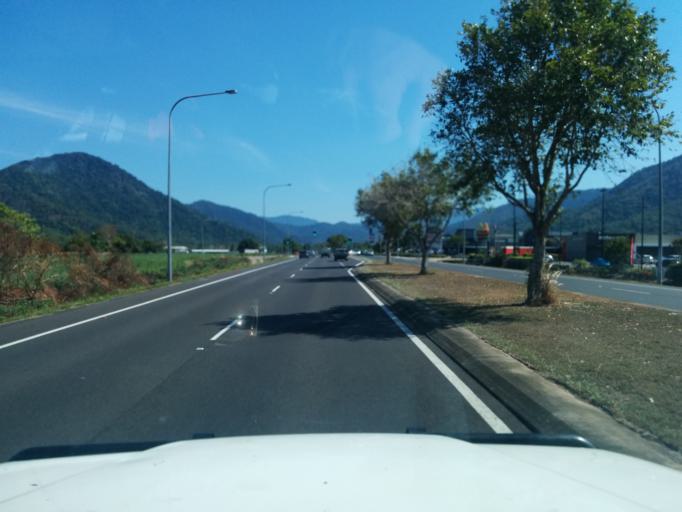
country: AU
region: Queensland
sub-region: Cairns
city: Redlynch
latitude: -16.8938
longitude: 145.7005
